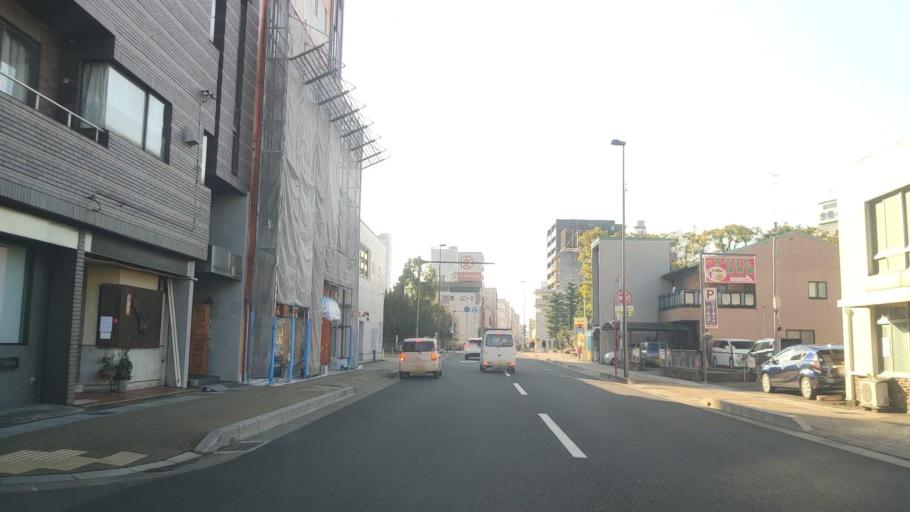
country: JP
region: Gifu
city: Gifu-shi
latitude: 35.4119
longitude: 136.7650
